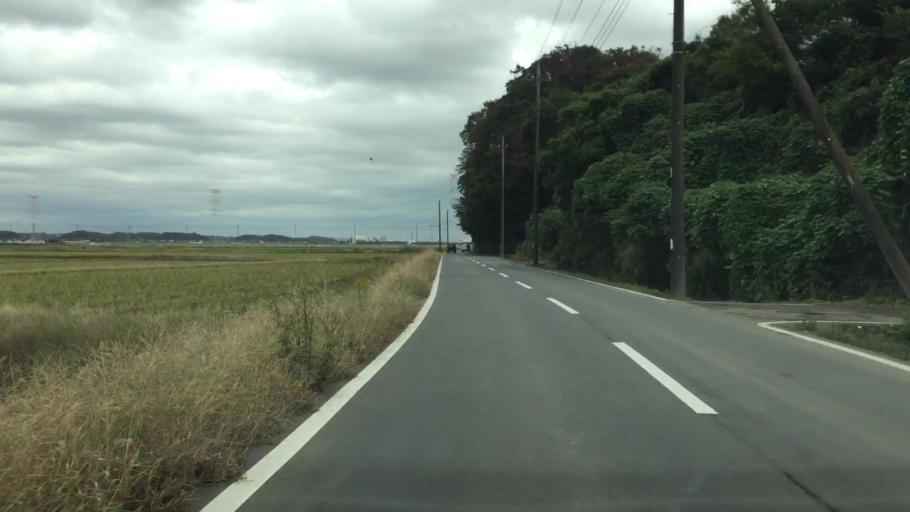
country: JP
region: Chiba
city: Shiroi
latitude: 35.8434
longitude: 140.0915
